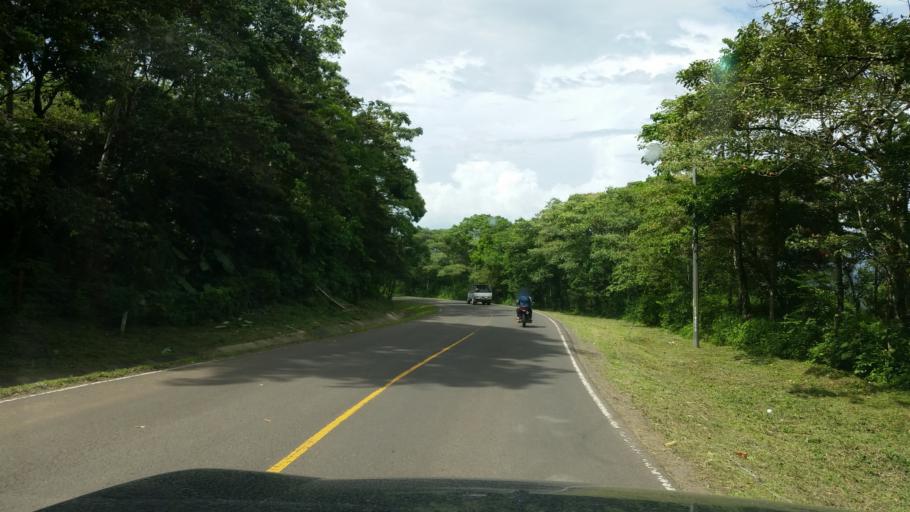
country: NI
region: Matagalpa
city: San Ramon
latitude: 12.9647
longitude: -85.8548
